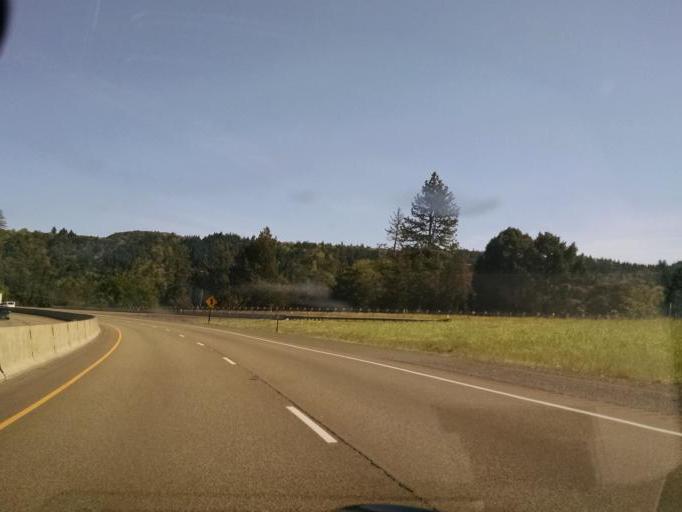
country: US
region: Oregon
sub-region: Douglas County
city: Riddle
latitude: 42.9492
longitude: -123.3298
